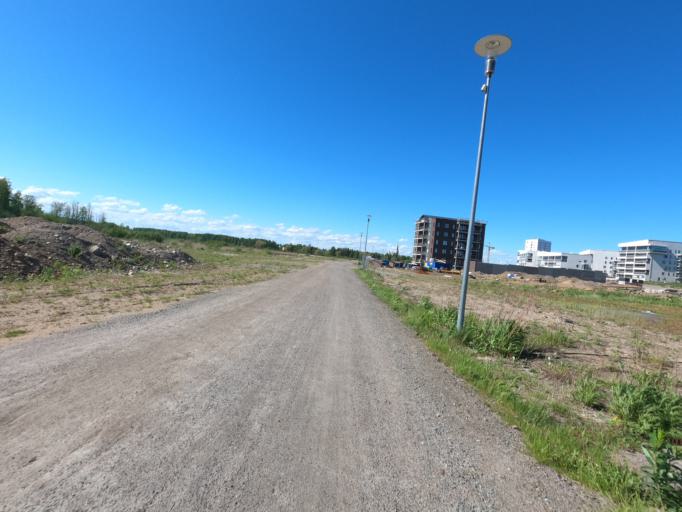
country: FI
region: North Karelia
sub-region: Joensuu
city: Joensuu
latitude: 62.5882
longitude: 29.7611
